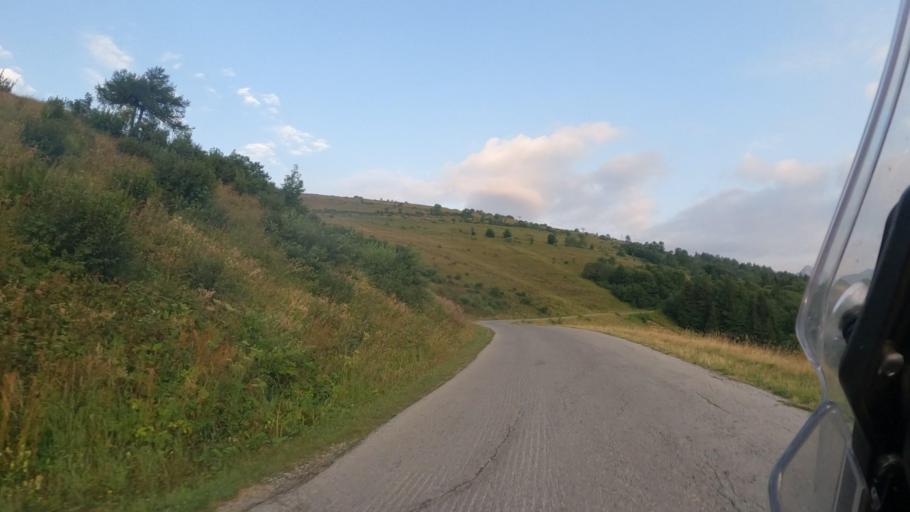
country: IT
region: Piedmont
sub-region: Provincia di Cuneo
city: Limone Piemonte
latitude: 44.1594
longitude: 7.5686
